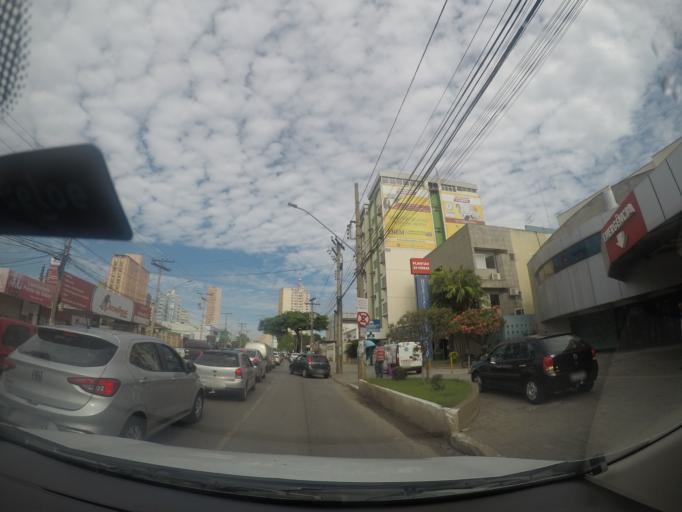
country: BR
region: Goias
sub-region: Goiania
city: Goiania
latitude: -16.6703
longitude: -49.2562
